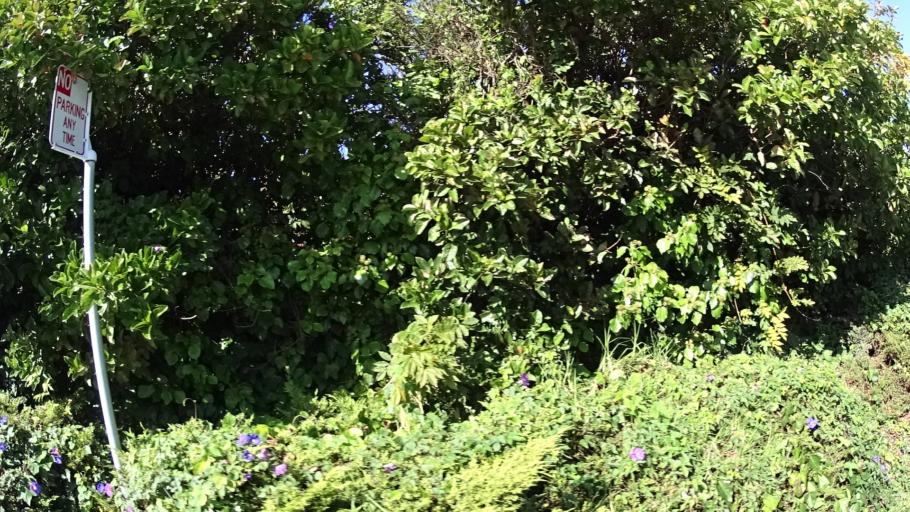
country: US
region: California
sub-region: San Mateo County
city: Millbrae
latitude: 37.5942
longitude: -122.4064
